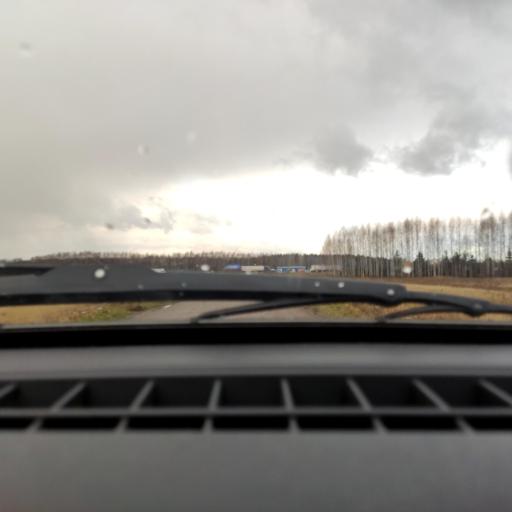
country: RU
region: Bashkortostan
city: Iglino
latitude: 54.7436
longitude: 56.3173
